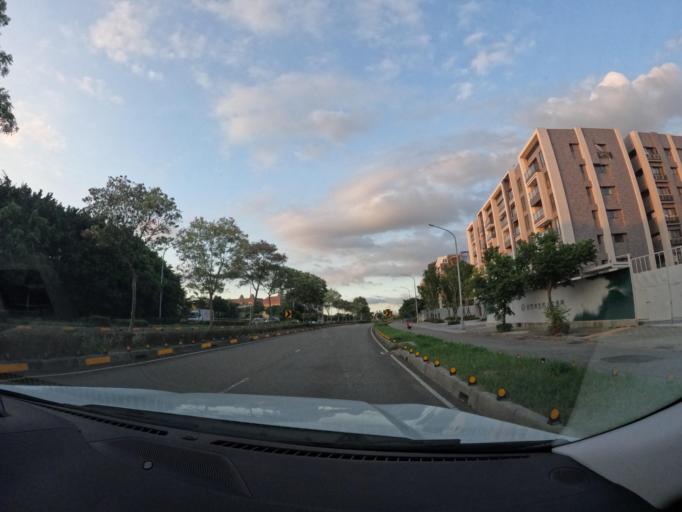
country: TW
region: Taiwan
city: Taoyuan City
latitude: 25.0226
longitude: 121.2159
